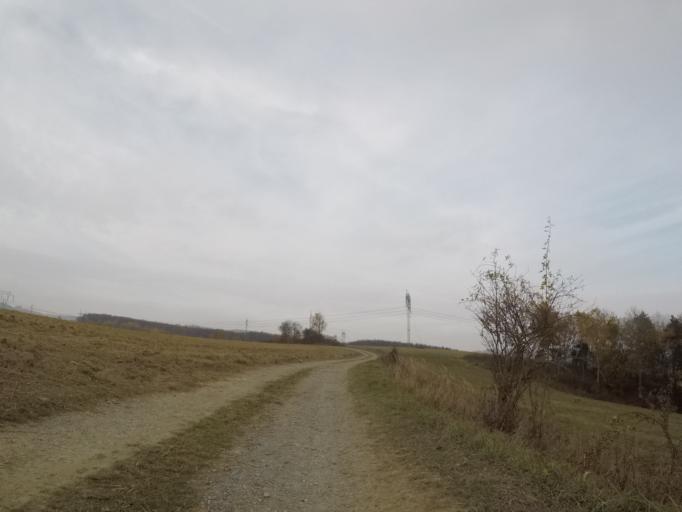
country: SK
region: Presovsky
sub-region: Okres Presov
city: Presov
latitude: 48.9051
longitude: 21.1587
